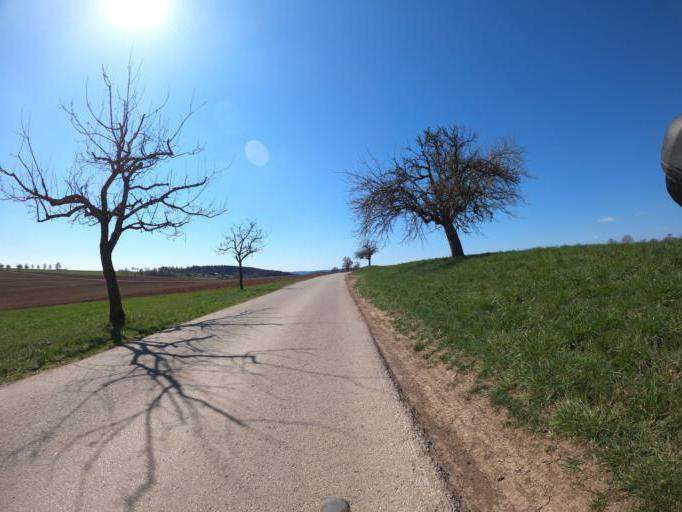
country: DE
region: Baden-Wuerttemberg
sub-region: Karlsruhe Region
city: Horb am Neckar
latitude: 48.4120
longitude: 8.6753
